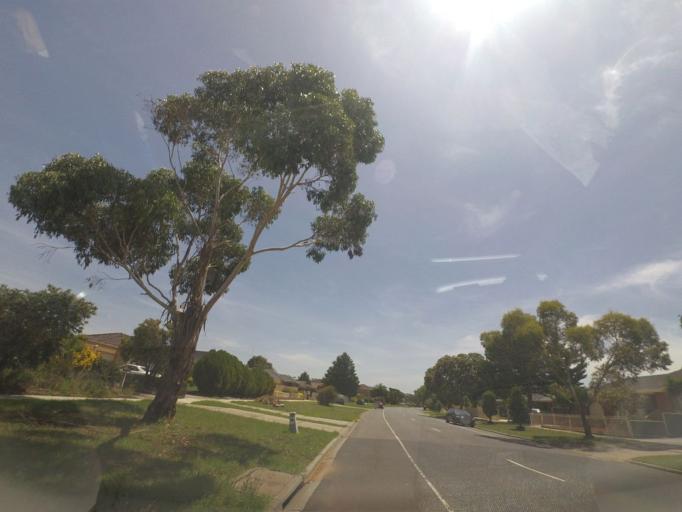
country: AU
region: Victoria
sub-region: Brimbank
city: Keilor Downs
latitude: -37.7226
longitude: 144.8029
